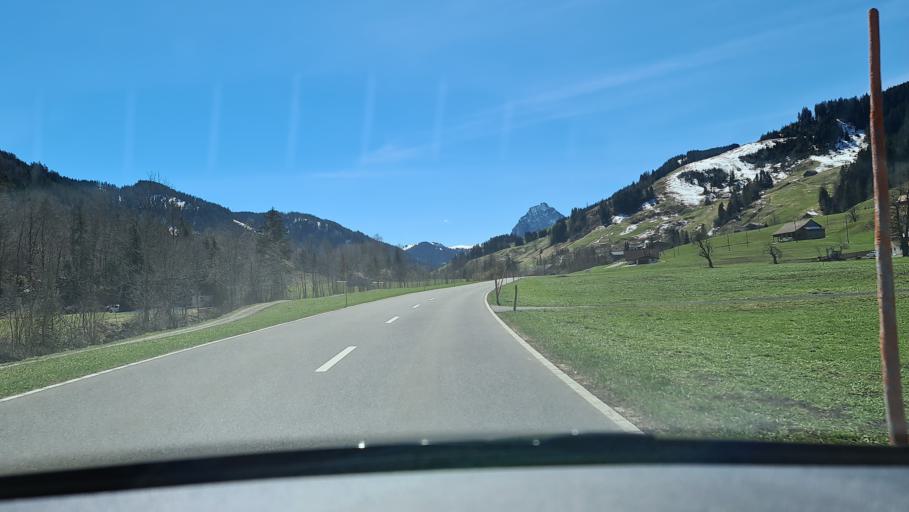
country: CH
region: Schwyz
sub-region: Bezirk Einsiedeln
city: Einsiedeln
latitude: 47.0928
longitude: 8.7258
